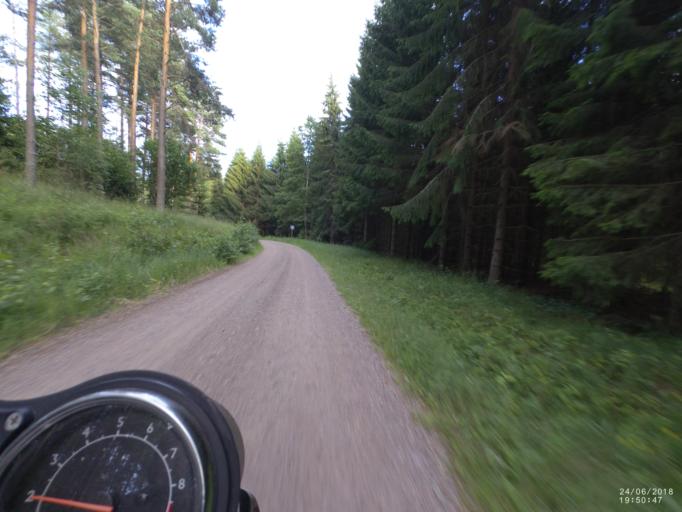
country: SE
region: Soedermanland
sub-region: Oxelosunds Kommun
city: Oxelosund
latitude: 58.7747
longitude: 17.1488
